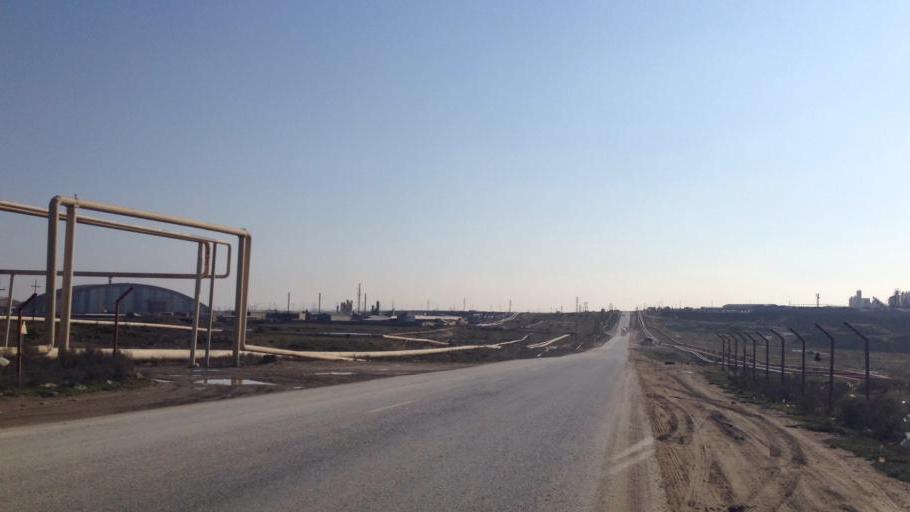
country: AZ
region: Abseron
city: Digah
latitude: 40.4701
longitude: 49.8850
